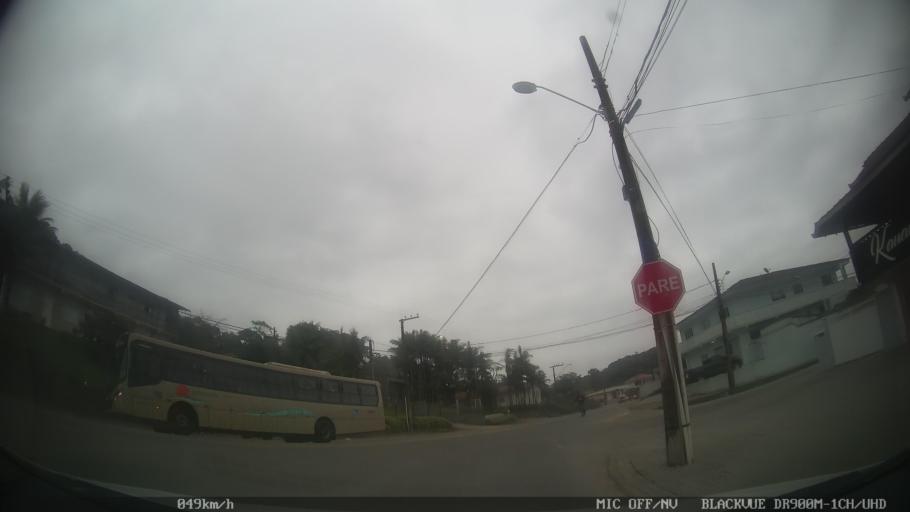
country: BR
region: Santa Catarina
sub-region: Joinville
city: Joinville
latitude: -26.3673
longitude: -48.8351
